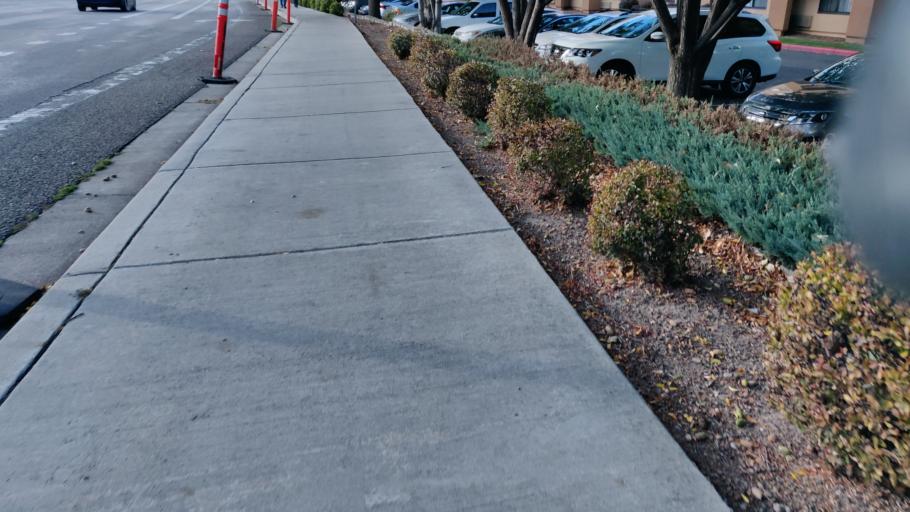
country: US
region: Idaho
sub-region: Ada County
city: Boise
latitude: 43.6073
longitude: -116.1916
